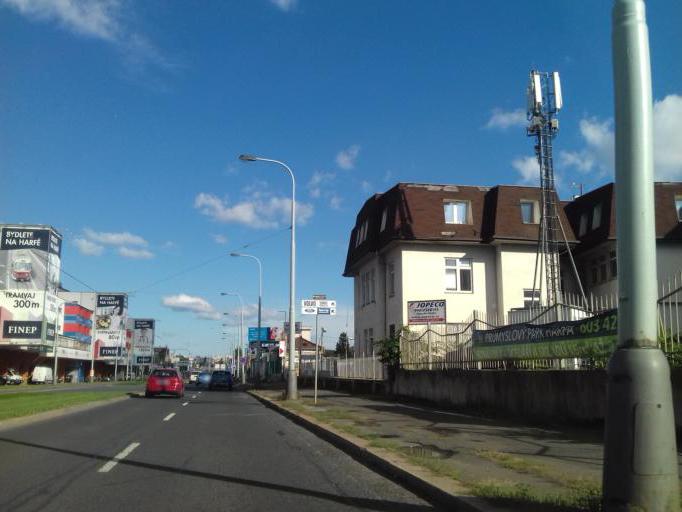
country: CZ
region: Praha
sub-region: Praha 9
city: Vysocany
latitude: 50.1025
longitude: 14.5096
